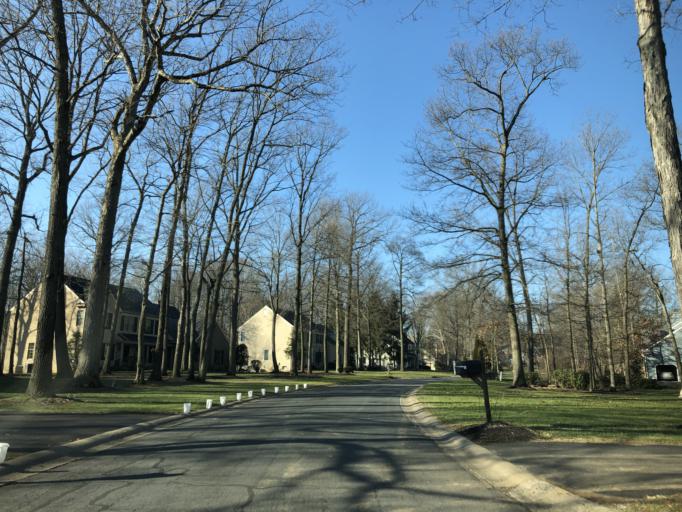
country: US
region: Pennsylvania
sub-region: Chester County
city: Downingtown
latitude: 39.9870
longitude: -75.6962
